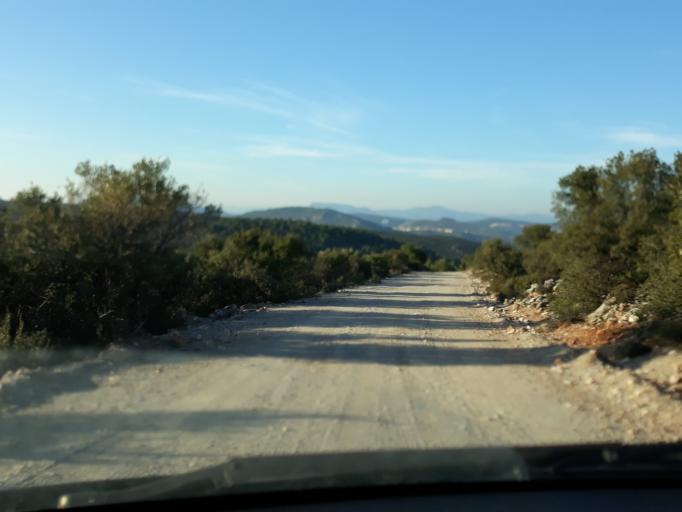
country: GR
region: Central Greece
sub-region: Nomos Voiotias
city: Asopia
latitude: 38.2493
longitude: 23.5317
